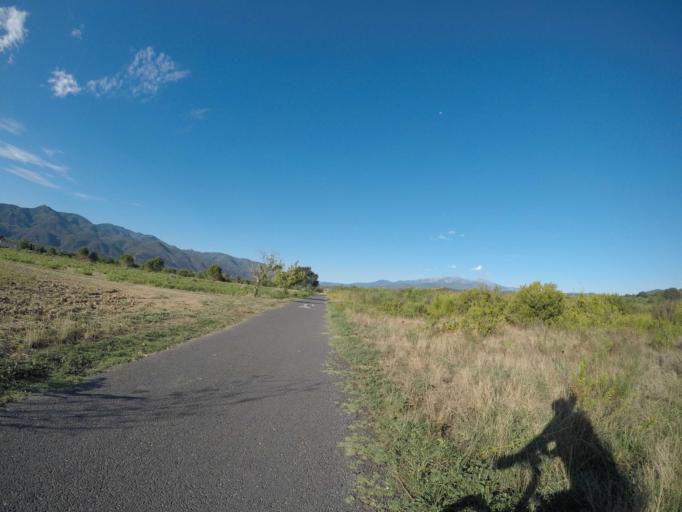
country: FR
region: Languedoc-Roussillon
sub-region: Departement des Pyrenees-Orientales
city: Sant Joan de Pladecorts
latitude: 42.5141
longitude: 2.7793
